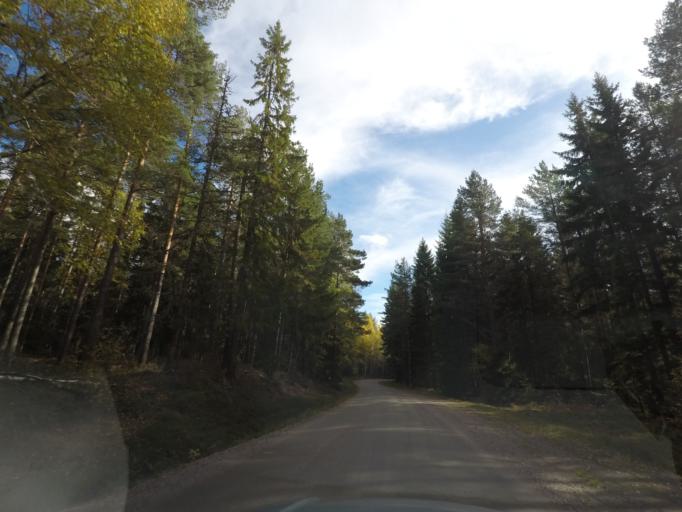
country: SE
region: Vaestmanland
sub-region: Kungsors Kommun
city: Kungsoer
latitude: 59.3348
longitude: 16.2172
